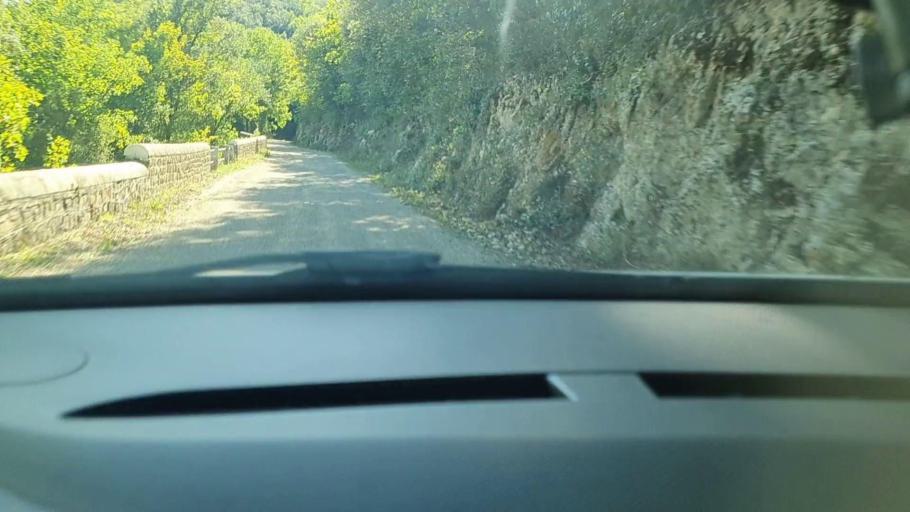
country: FR
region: Languedoc-Roussillon
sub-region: Departement du Gard
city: Saint-Ambroix
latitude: 44.2183
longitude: 4.2924
